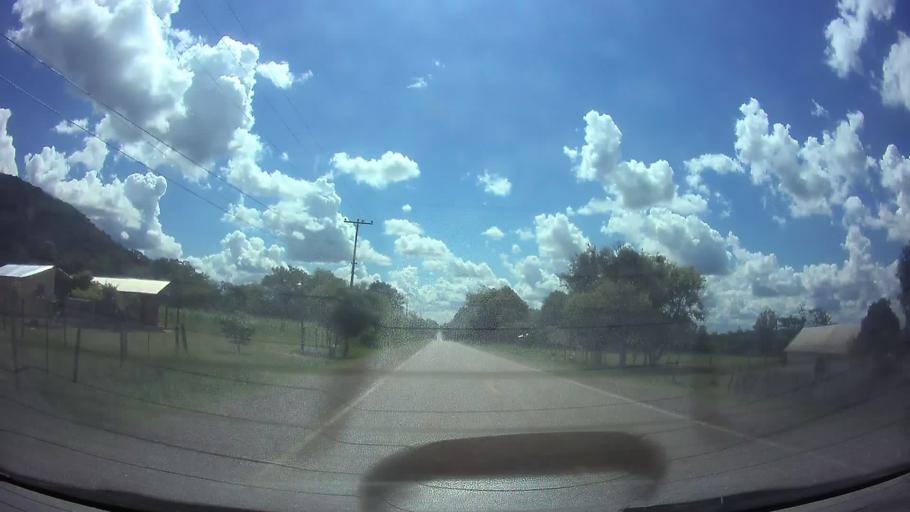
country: PY
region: Paraguari
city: La Colmena
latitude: -25.9141
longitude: -56.7468
